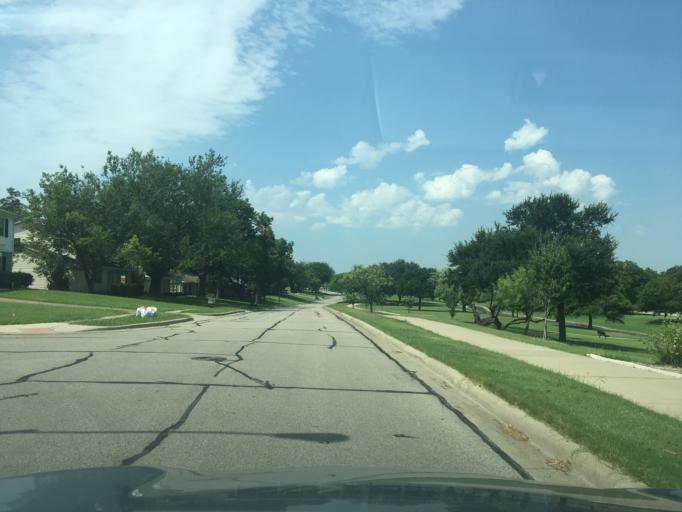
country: US
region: Texas
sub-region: Dallas County
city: Farmers Branch
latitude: 32.9305
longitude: -96.8777
